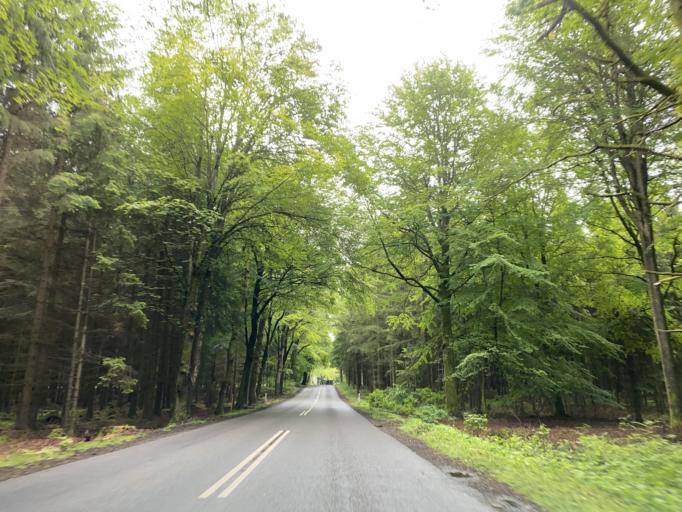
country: DK
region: Central Jutland
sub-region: Favrskov Kommune
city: Hammel
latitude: 56.2589
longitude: 9.9485
